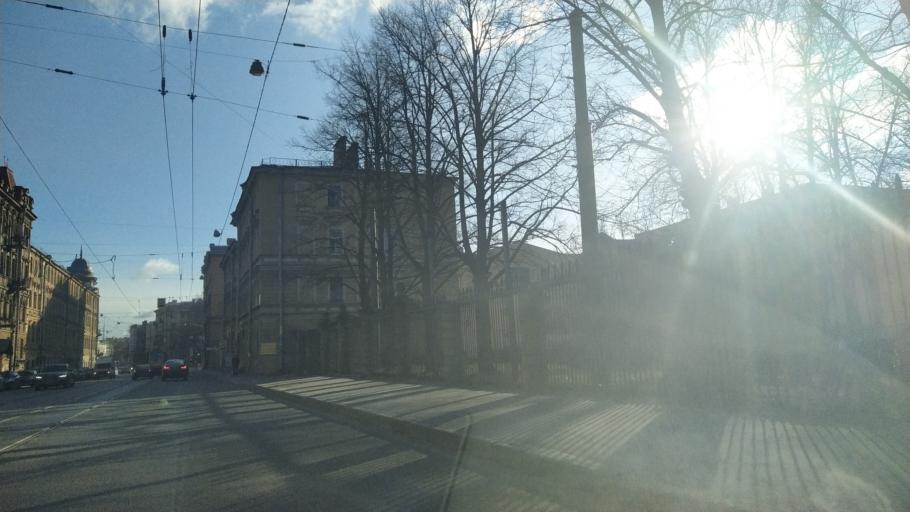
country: RU
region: Leningrad
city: Finlyandskiy
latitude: 59.9641
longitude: 30.3513
